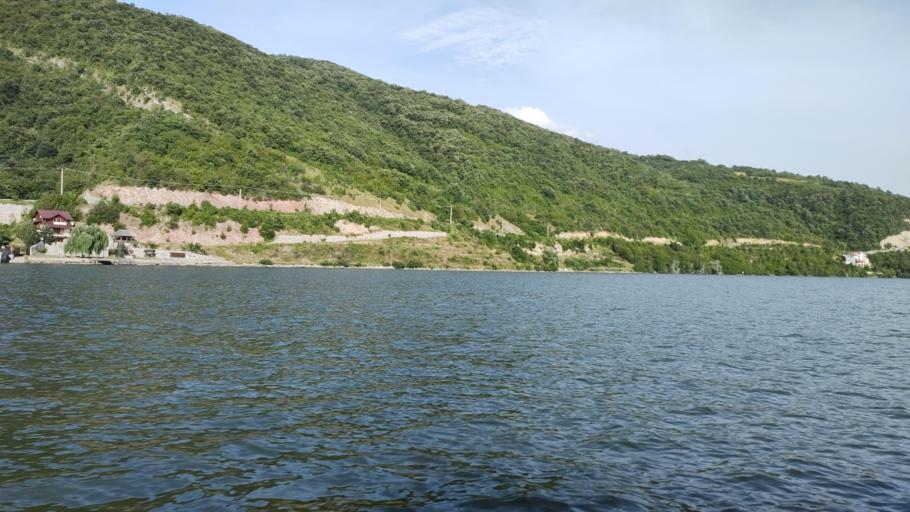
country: RO
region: Mehedinti
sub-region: Comuna Svinita
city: Svinita
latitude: 44.5196
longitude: 22.0748
